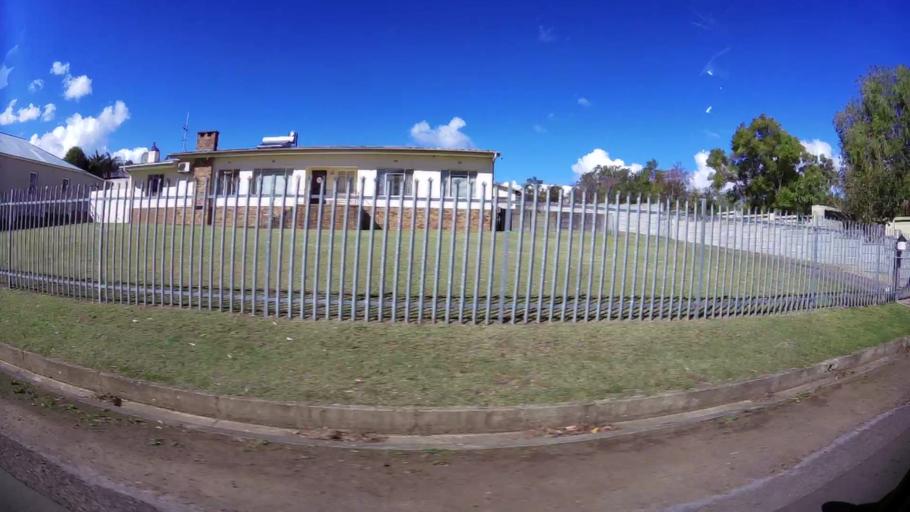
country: ZA
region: Western Cape
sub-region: Overberg District Municipality
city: Swellendam
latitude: -34.0245
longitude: 20.4464
